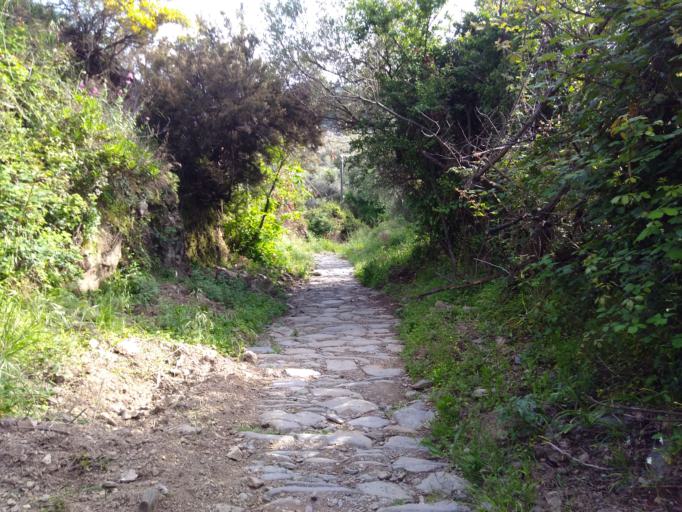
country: IT
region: Liguria
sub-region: Provincia di La Spezia
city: Monterosso al Mare
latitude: 44.1515
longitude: 9.6553
